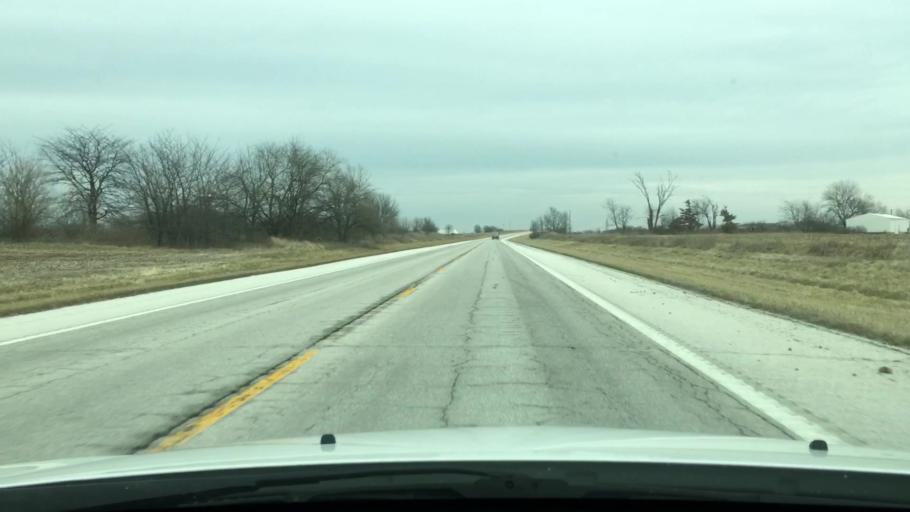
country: US
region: Missouri
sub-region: Pike County
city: Bowling Green
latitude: 39.3509
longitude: -91.2217
